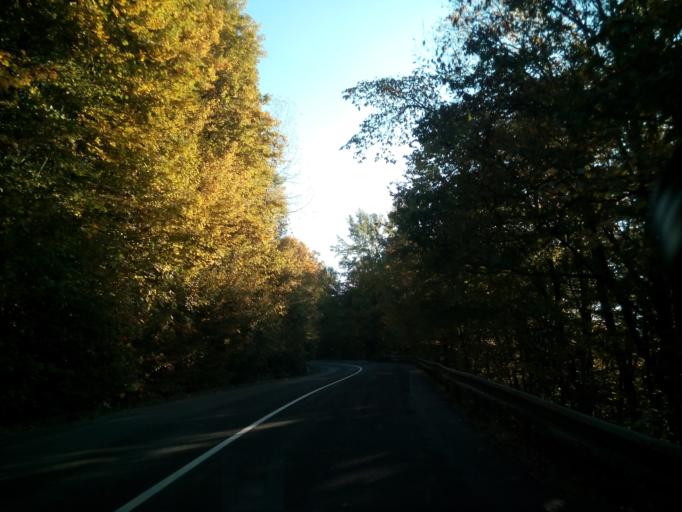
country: SK
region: Kosicky
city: Gelnica
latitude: 48.8346
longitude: 21.0528
